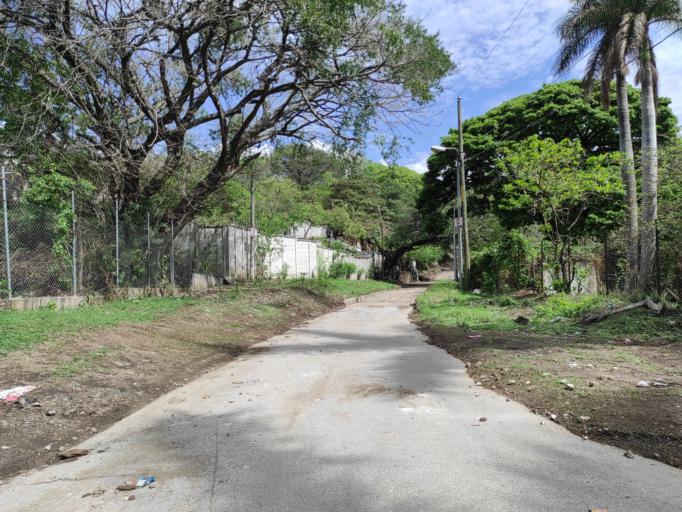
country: GT
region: Guatemala
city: Amatitlan
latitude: 14.4827
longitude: -90.6099
